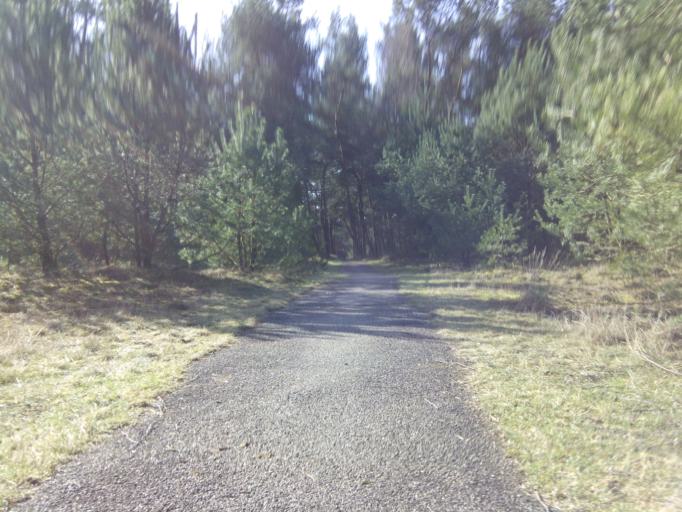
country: NL
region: Gelderland
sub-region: Gemeente Ede
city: Harskamp
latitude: 52.1589
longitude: 5.7346
